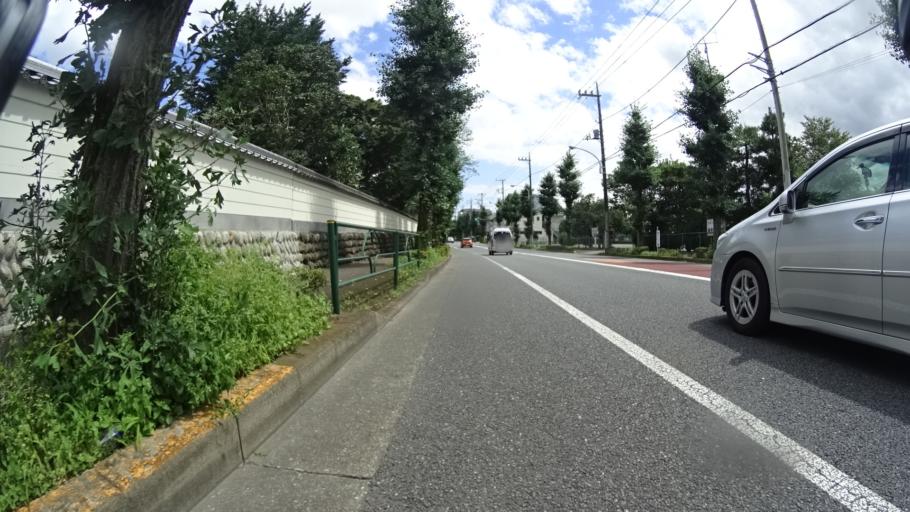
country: JP
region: Tokyo
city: Fussa
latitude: 35.7519
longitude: 139.3179
